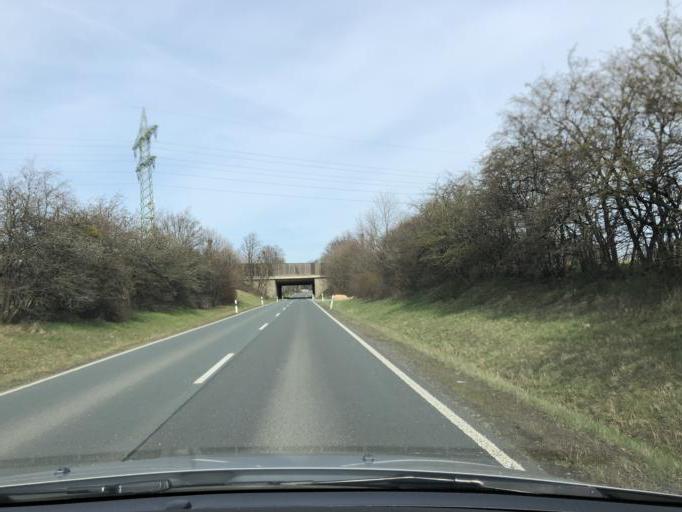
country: DE
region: Thuringia
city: Eisenberg
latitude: 50.9836
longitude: 11.8994
